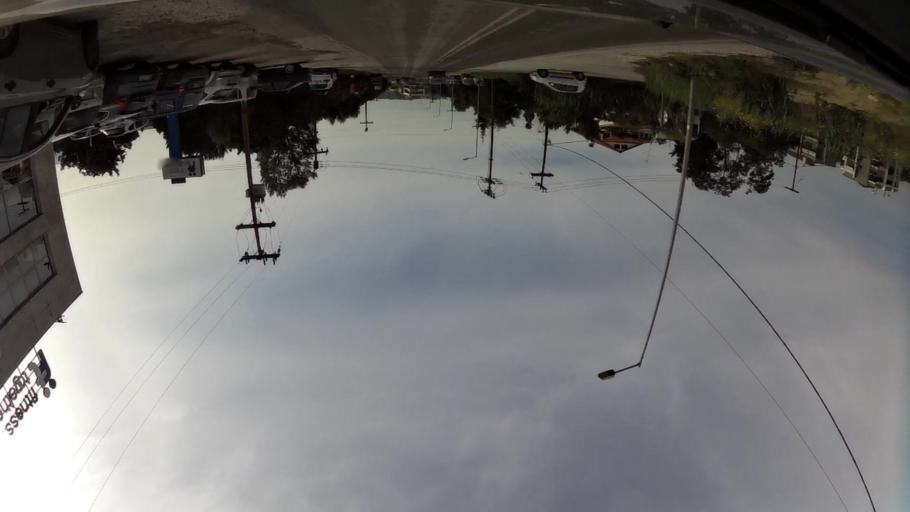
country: GR
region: Central Macedonia
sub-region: Nomos Thessalonikis
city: Thermi
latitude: 40.5548
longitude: 23.0189
